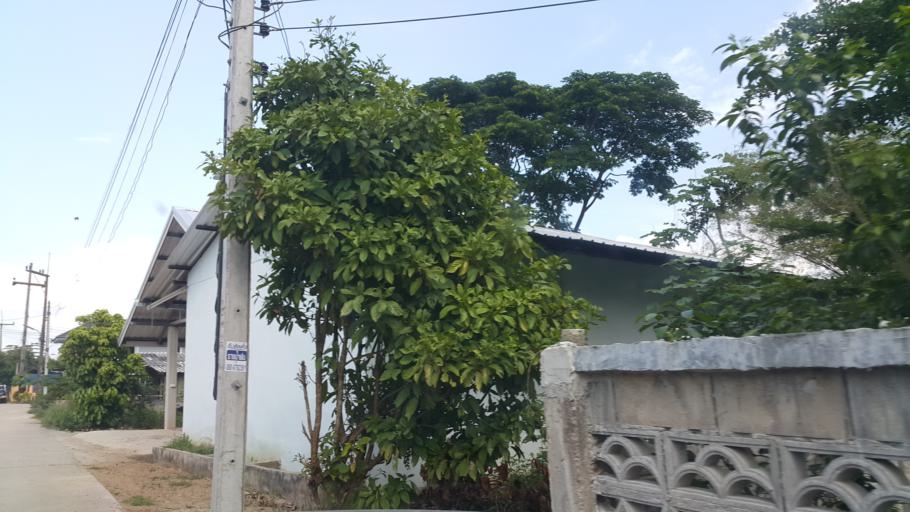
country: TH
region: Chiang Rai
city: Wiang Chai
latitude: 19.9088
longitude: 99.8971
